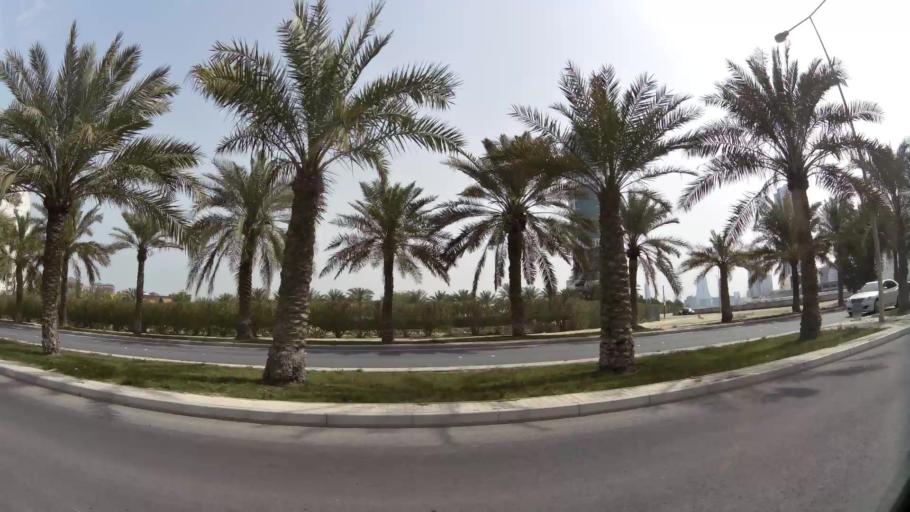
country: BH
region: Manama
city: Jidd Hafs
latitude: 26.2386
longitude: 50.5419
